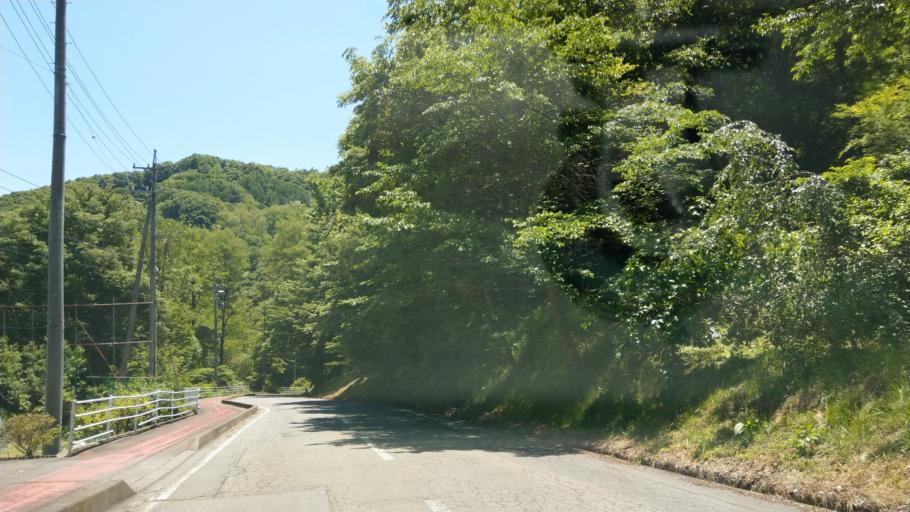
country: JP
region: Nagano
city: Komoro
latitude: 36.3263
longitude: 138.4028
